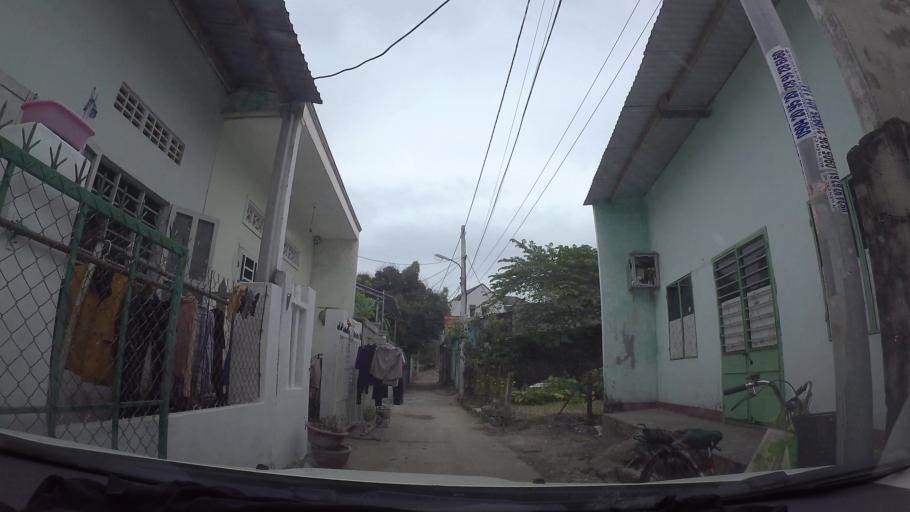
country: VN
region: Da Nang
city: Lien Chieu
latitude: 16.1036
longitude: 108.1314
